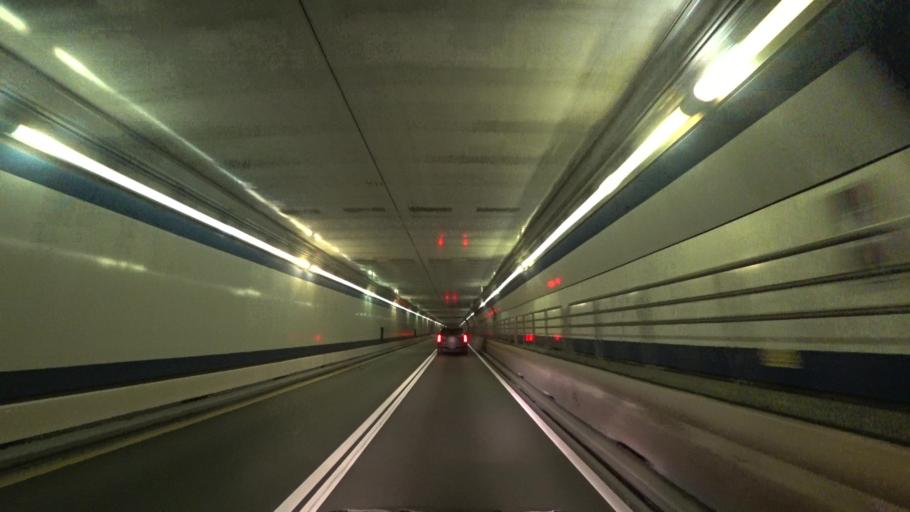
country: US
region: Massachusetts
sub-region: Suffolk County
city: Boston
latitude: 42.3678
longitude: -71.0463
